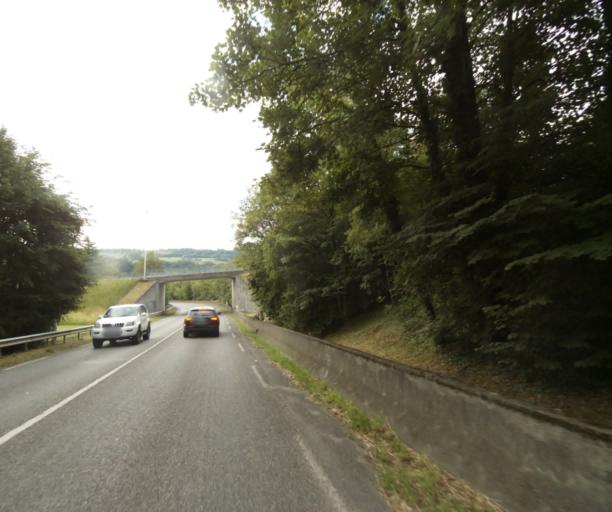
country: FR
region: Rhone-Alpes
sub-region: Departement de la Haute-Savoie
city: Thonon-les-Bains
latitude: 46.3793
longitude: 6.5001
